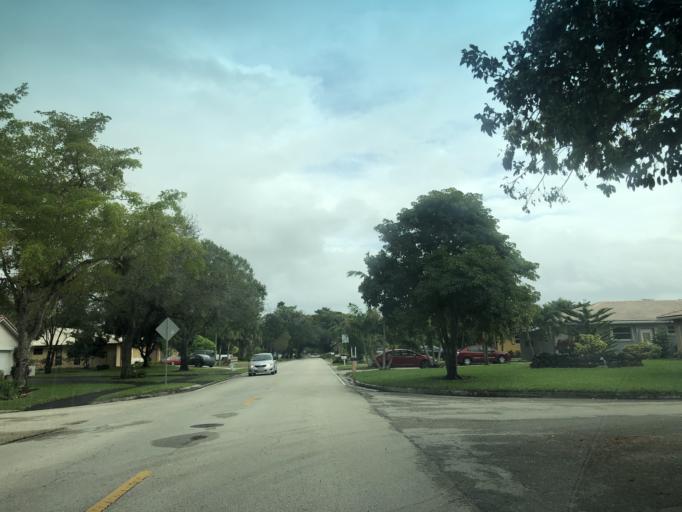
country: US
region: Florida
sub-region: Broward County
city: Coral Springs
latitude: 26.2480
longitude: -80.2507
